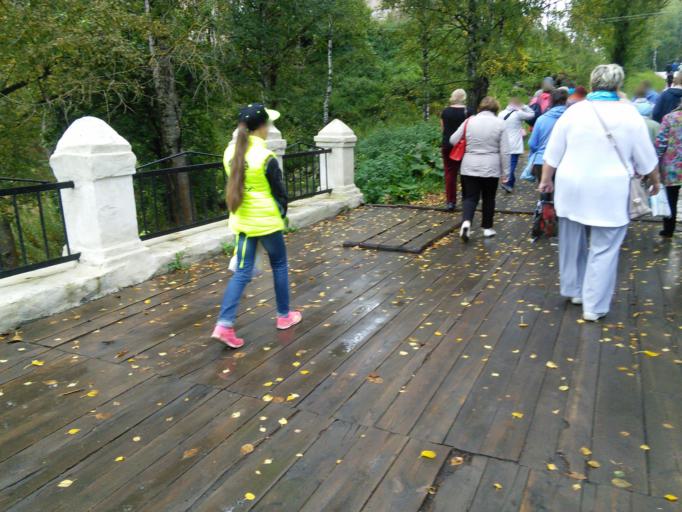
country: RU
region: Jaroslavl
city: Tutayev
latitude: 57.8799
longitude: 39.5461
